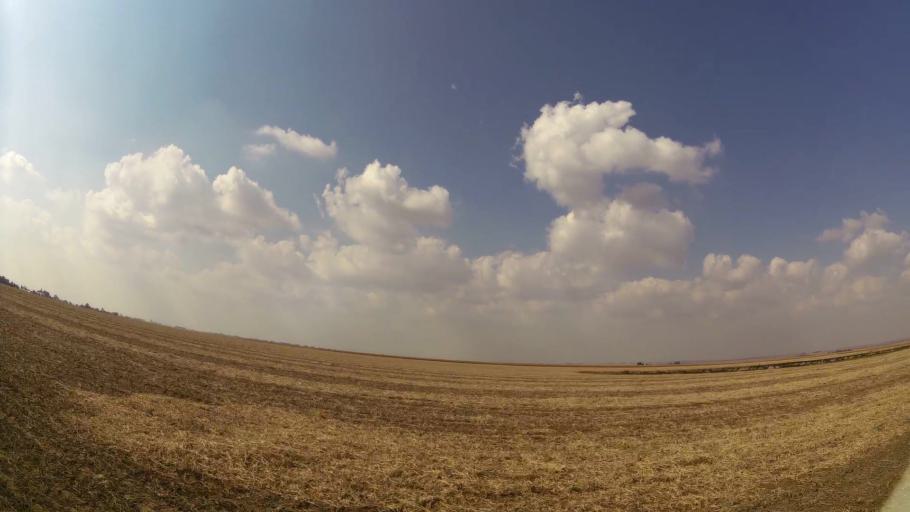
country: ZA
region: Mpumalanga
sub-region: Nkangala District Municipality
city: Delmas
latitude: -26.1953
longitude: 28.5473
